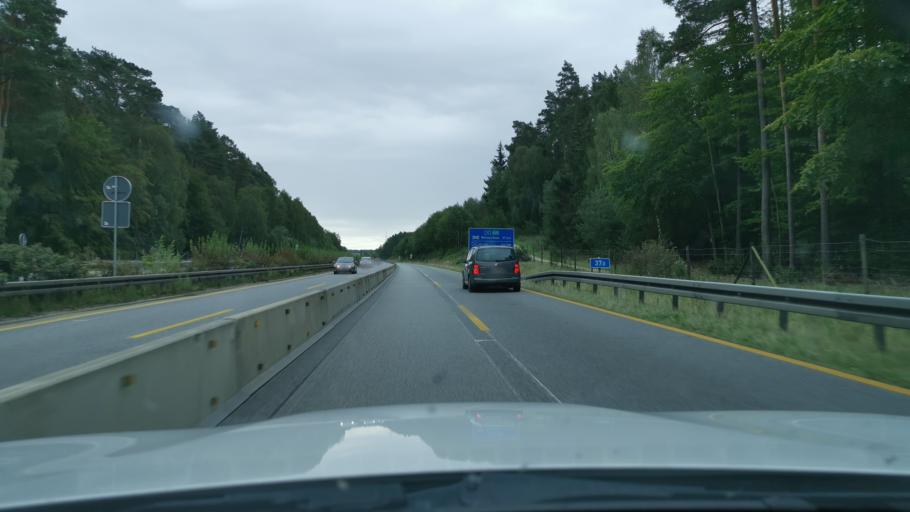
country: DE
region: Mecklenburg-Vorpommern
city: Malchow
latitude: 53.4491
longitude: 12.3933
